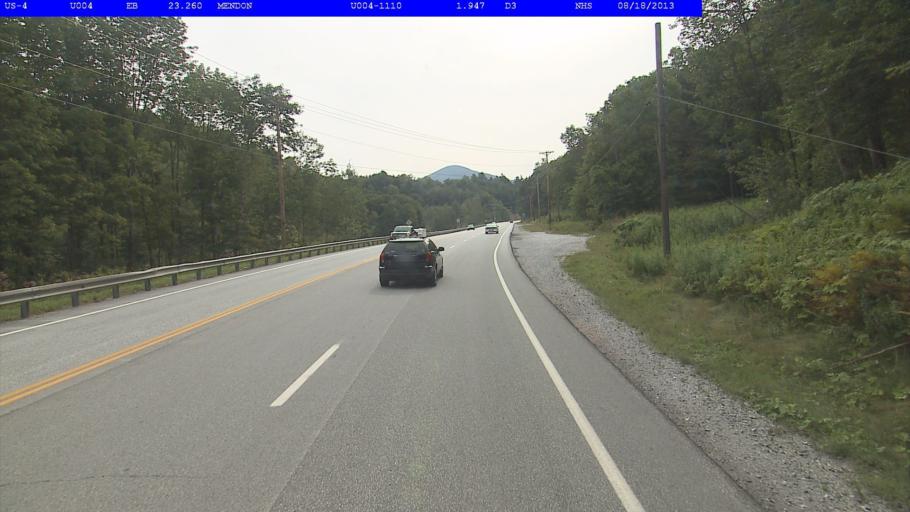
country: US
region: Vermont
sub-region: Rutland County
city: Rutland
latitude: 43.6512
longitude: -72.9144
